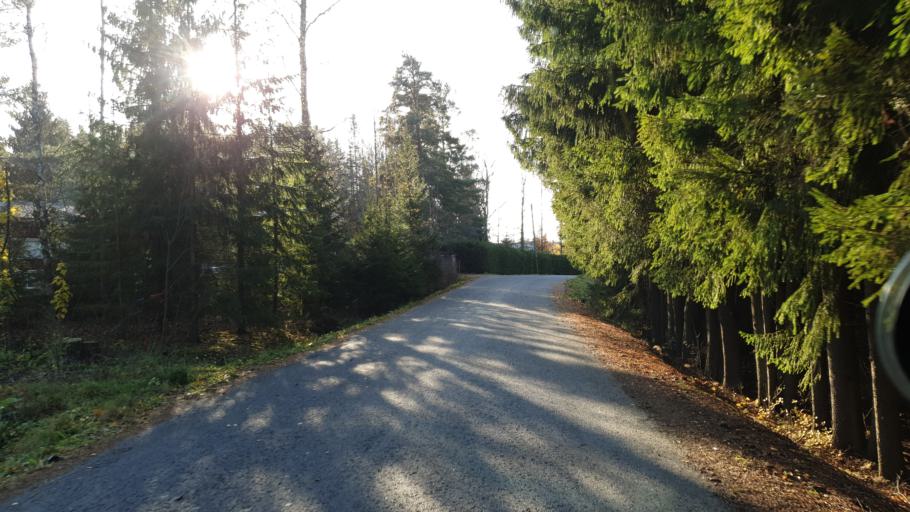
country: FI
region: Uusimaa
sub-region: Helsinki
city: Lohja
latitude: 60.2374
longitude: 24.1694
